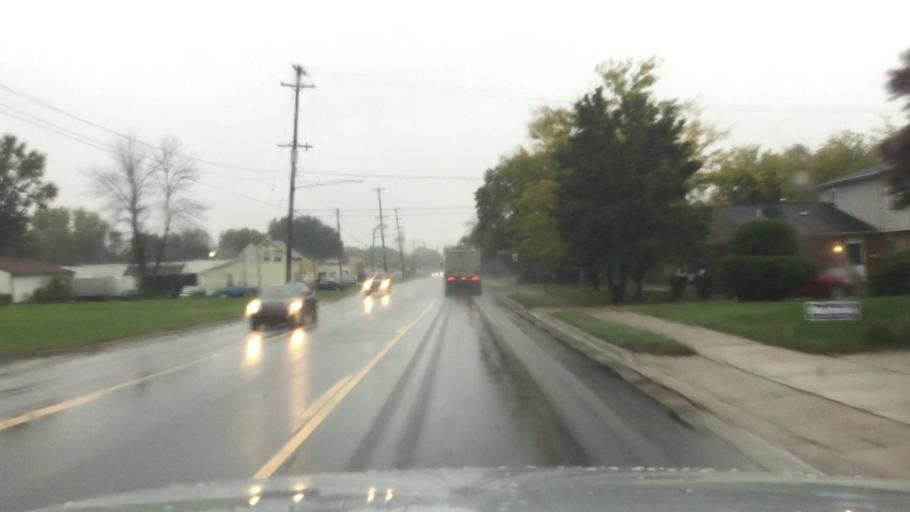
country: US
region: Michigan
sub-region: Saginaw County
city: Saginaw
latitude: 43.3938
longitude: -83.9556
